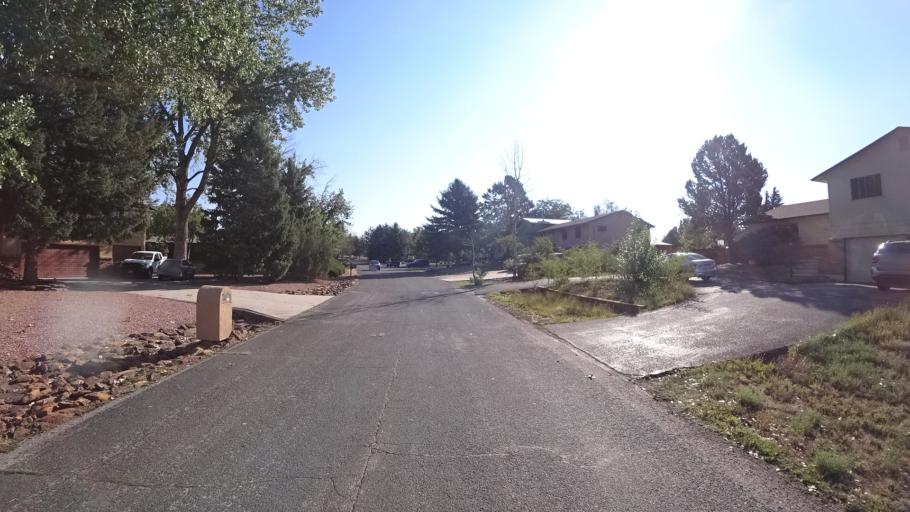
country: US
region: Colorado
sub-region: El Paso County
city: Air Force Academy
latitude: 38.9313
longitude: -104.7882
